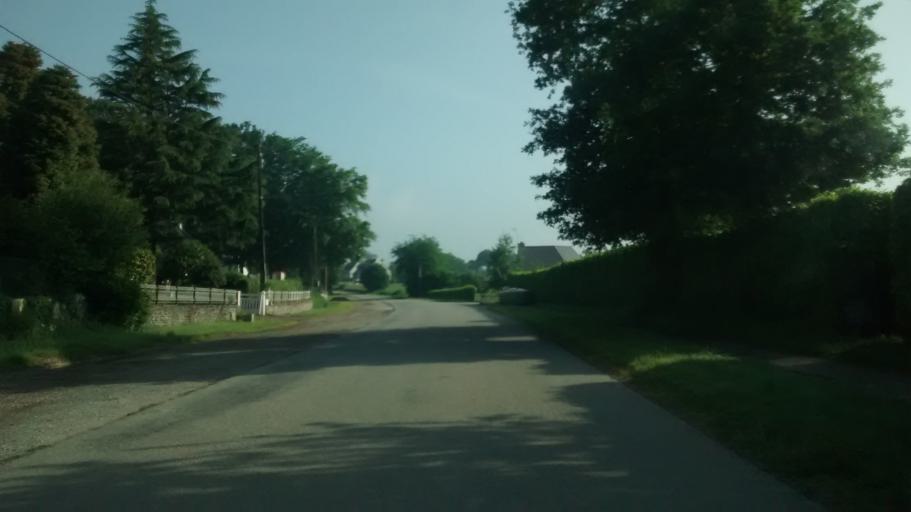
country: FR
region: Brittany
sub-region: Departement du Morbihan
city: Ruffiac
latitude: 47.8212
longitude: -2.2826
